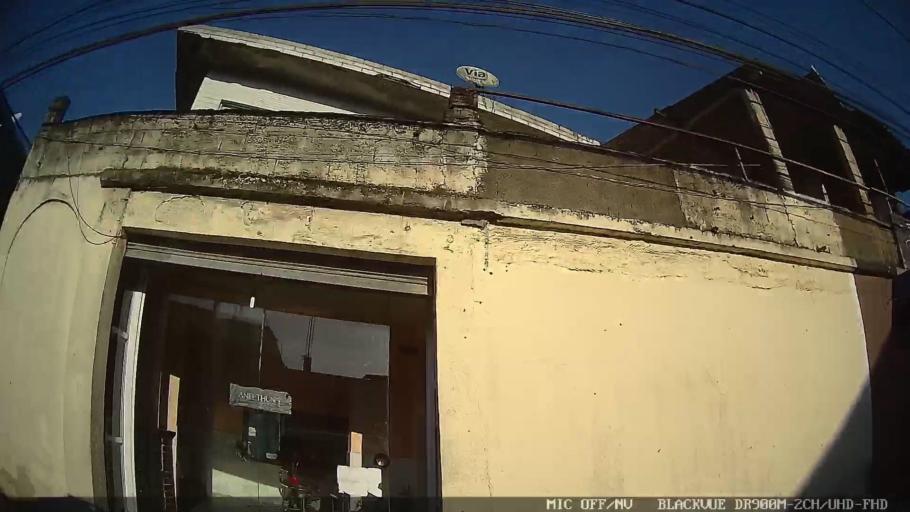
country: BR
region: Sao Paulo
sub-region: Guaruja
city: Guaruja
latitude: -23.9705
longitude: -46.2475
